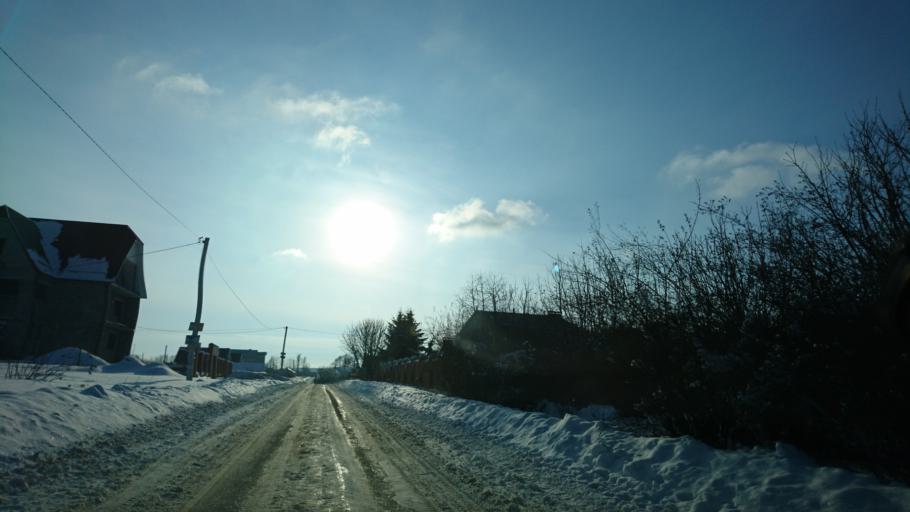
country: RU
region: Belgorod
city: Severnyy
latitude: 50.7251
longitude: 36.6114
